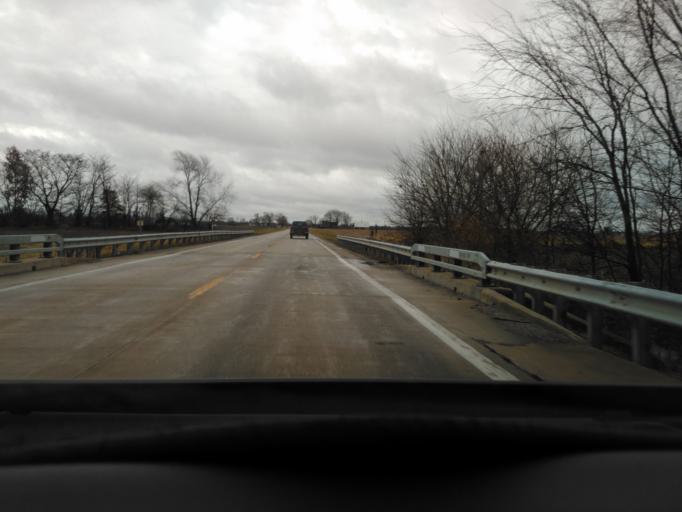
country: US
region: Illinois
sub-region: Effingham County
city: Altamont
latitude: 39.0460
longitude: -88.7774
